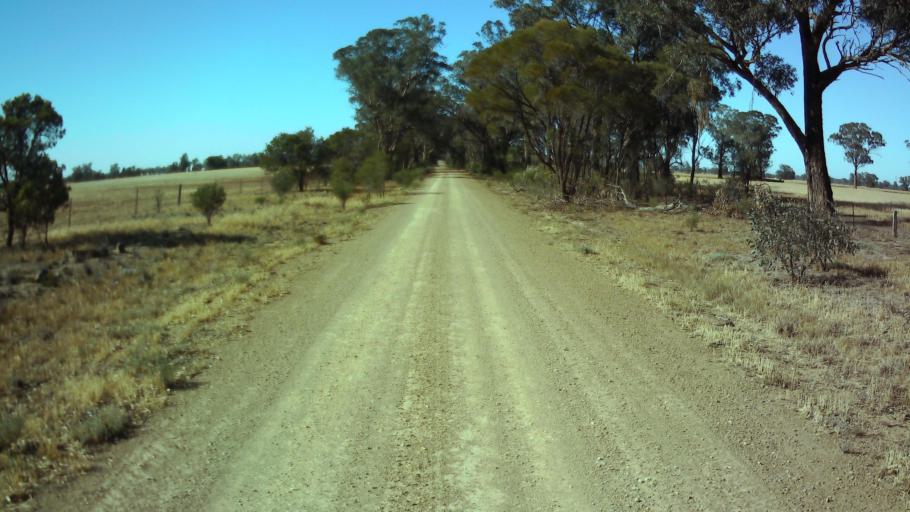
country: AU
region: New South Wales
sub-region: Weddin
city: Grenfell
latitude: -33.9193
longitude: 147.8751
